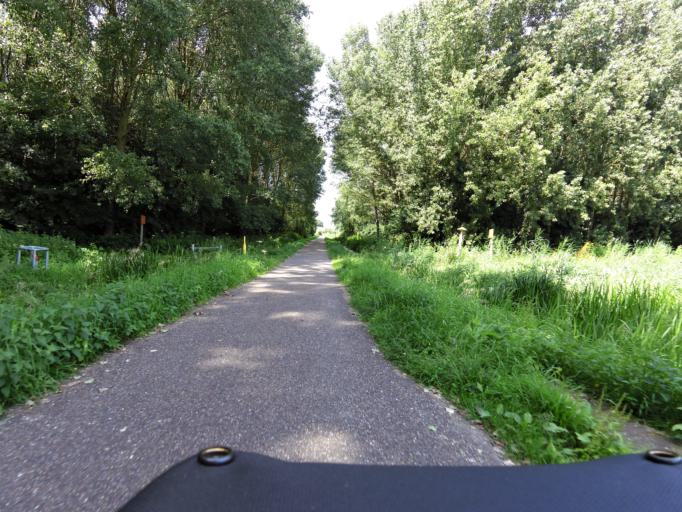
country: NL
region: South Holland
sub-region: Gemeente Albrandswaard
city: Rhoon
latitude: 51.8663
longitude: 4.3884
